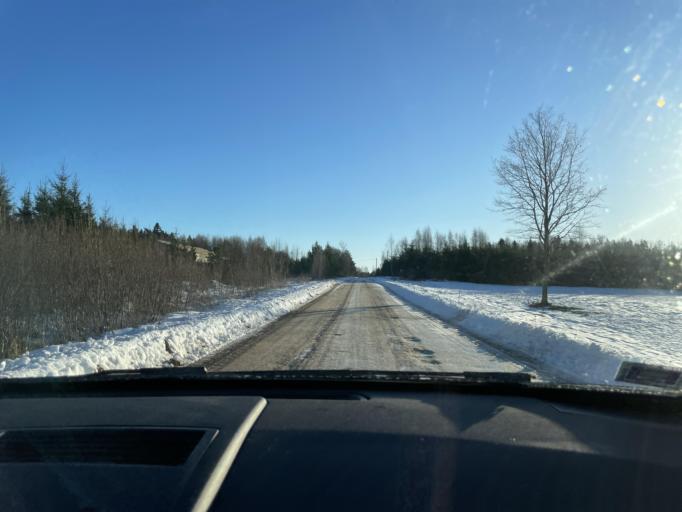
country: LV
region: Ludzas Rajons
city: Ludza
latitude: 56.4646
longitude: 27.6042
